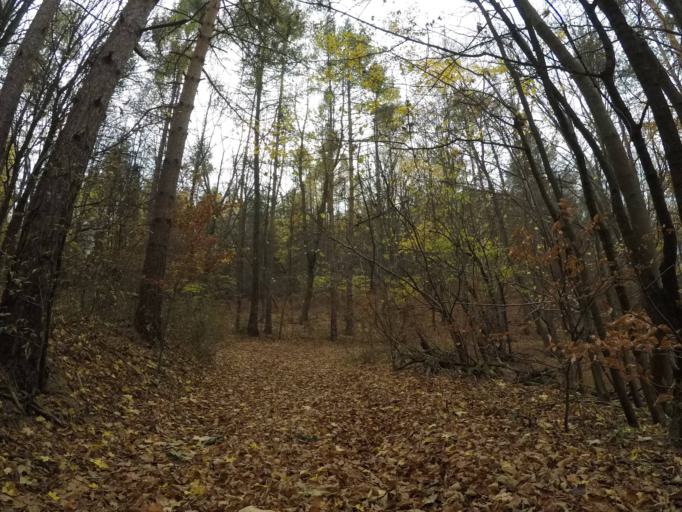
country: SK
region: Presovsky
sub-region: Okres Presov
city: Presov
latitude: 48.9014
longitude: 21.1672
